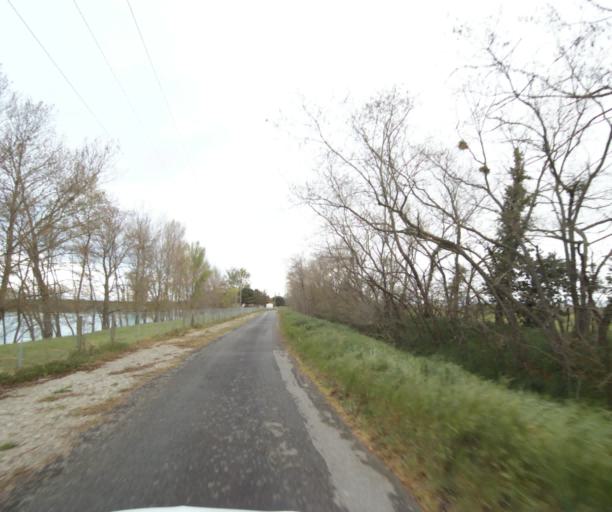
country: FR
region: Midi-Pyrenees
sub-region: Departement de l'Ariege
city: Saverdun
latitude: 43.2277
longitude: 1.6154
